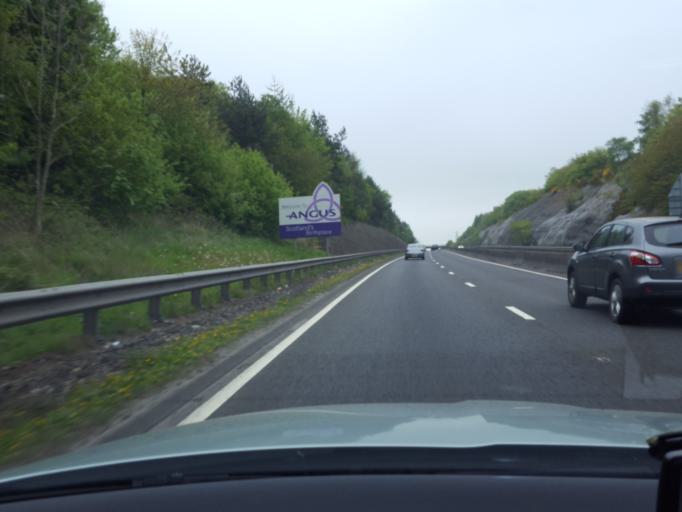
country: GB
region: Scotland
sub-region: Dundee City
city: Dundee
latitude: 56.4994
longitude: -2.9496
